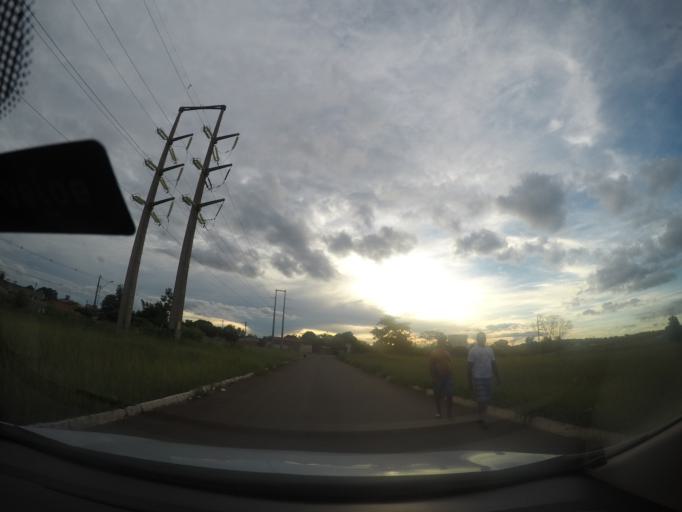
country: BR
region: Goias
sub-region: Goianira
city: Goianira
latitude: -16.5851
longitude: -49.3767
